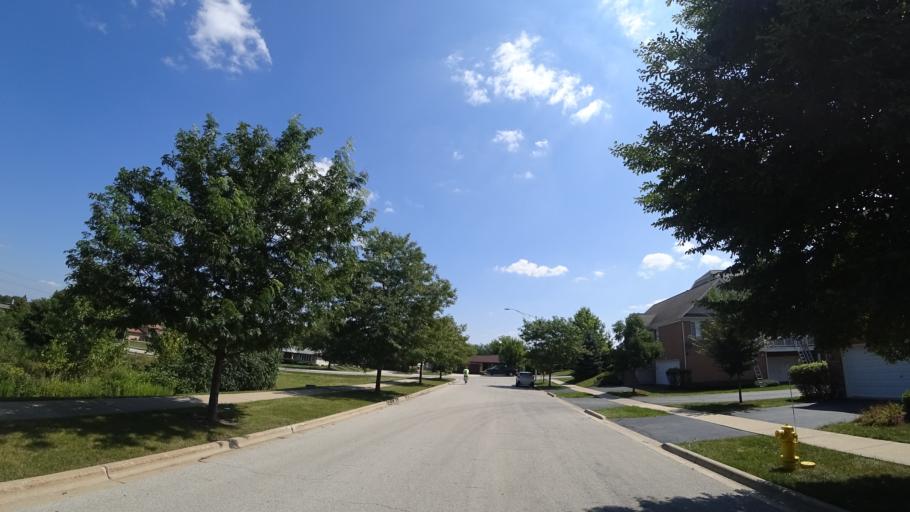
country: US
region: Illinois
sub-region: Cook County
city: Orland Park
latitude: 41.6366
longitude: -87.8499
